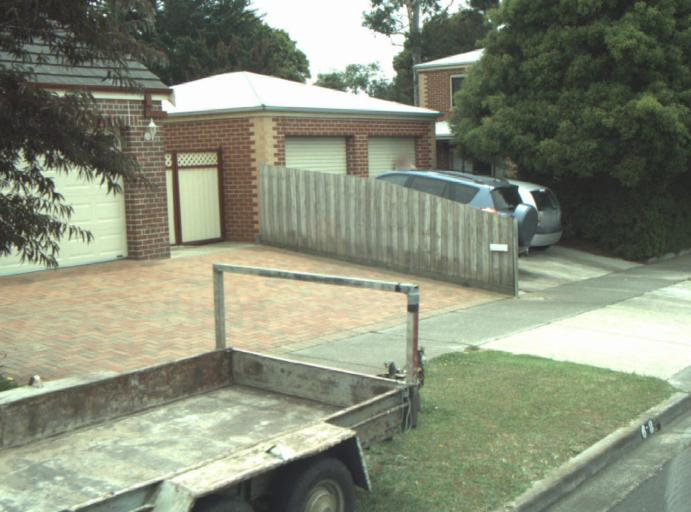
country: AU
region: Victoria
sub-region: Greater Geelong
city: Clifton Springs
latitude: -38.1659
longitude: 144.5761
